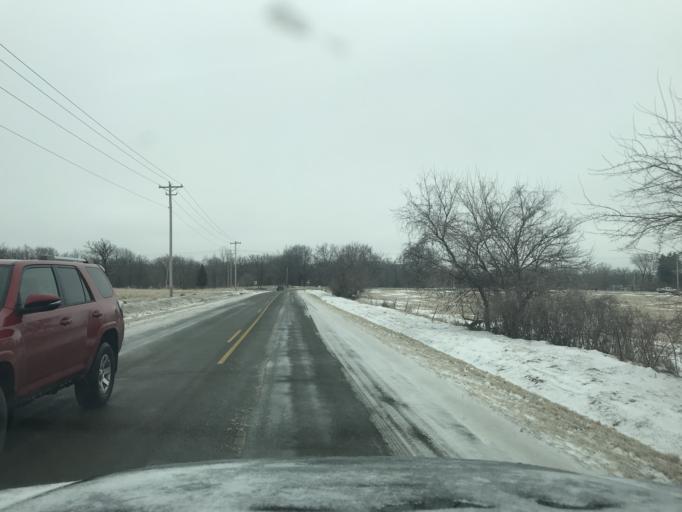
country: US
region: Wisconsin
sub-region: Dane County
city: Cottage Grove
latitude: 43.0914
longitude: -89.2295
